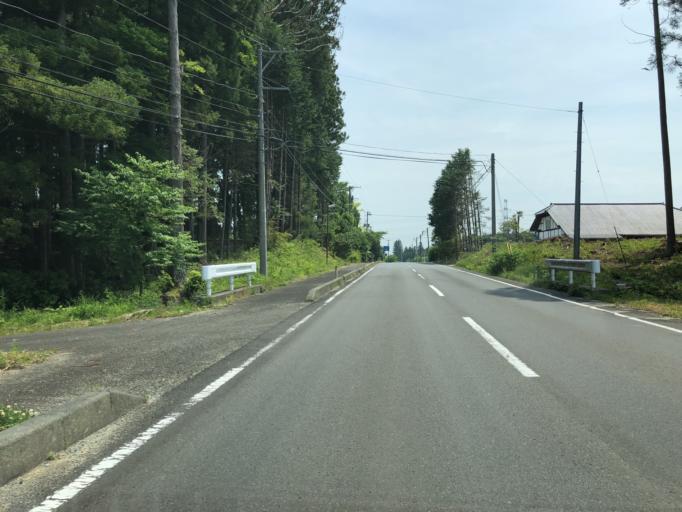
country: JP
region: Fukushima
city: Namie
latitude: 37.5368
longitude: 140.9377
